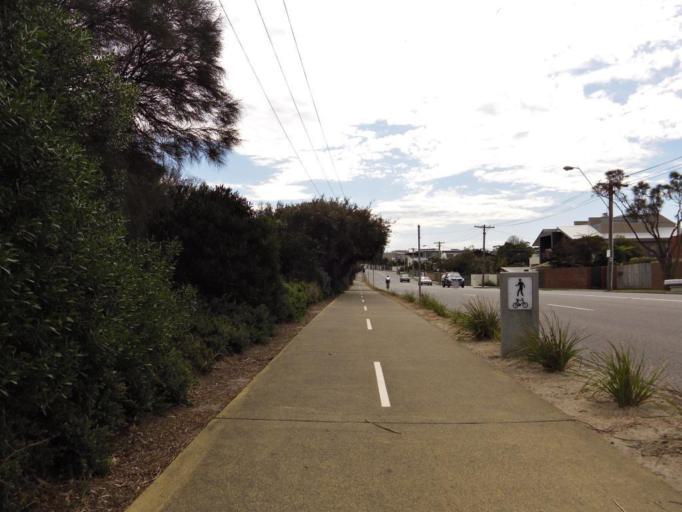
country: AU
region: Victoria
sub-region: Bayside
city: Black Rock
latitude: -37.9693
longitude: 145.0118
